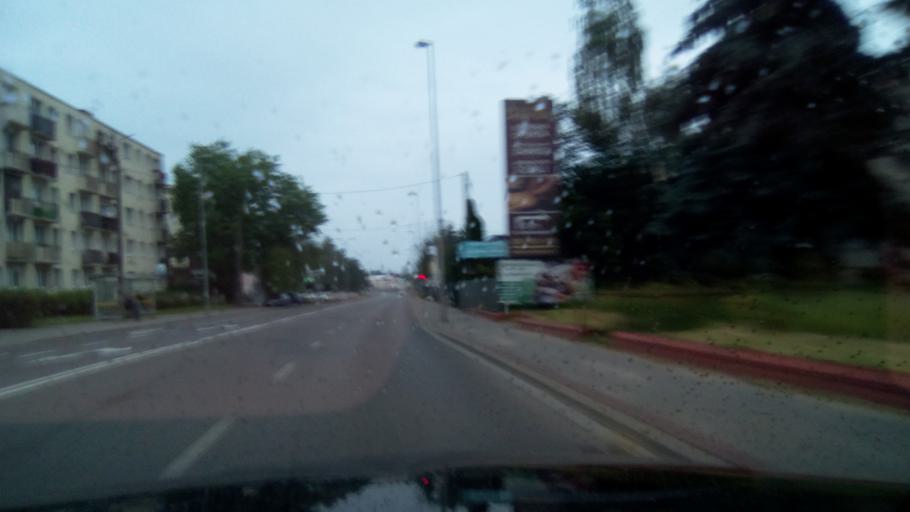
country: PL
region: Greater Poland Voivodeship
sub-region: Powiat poznanski
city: Swarzedz
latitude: 52.4130
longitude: 17.0853
